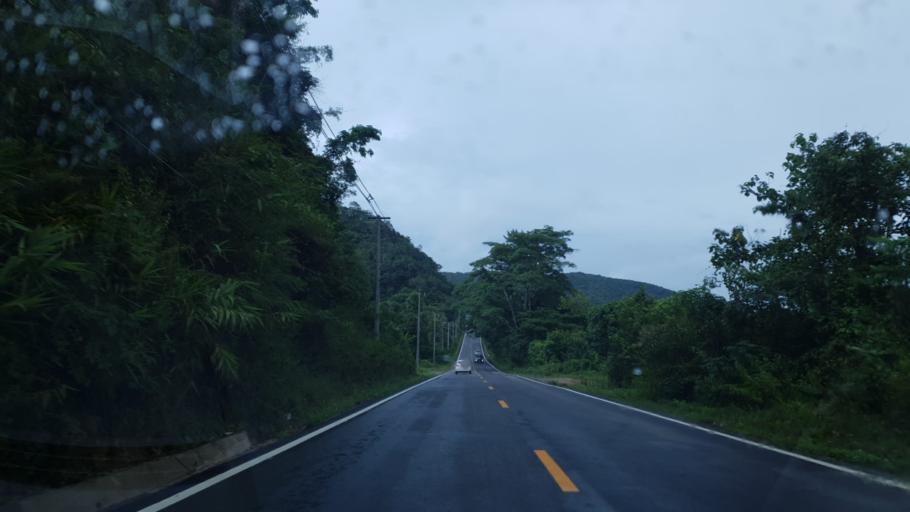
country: TH
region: Mae Hong Son
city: Ban Huai I Huak
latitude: 18.1447
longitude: 98.1170
